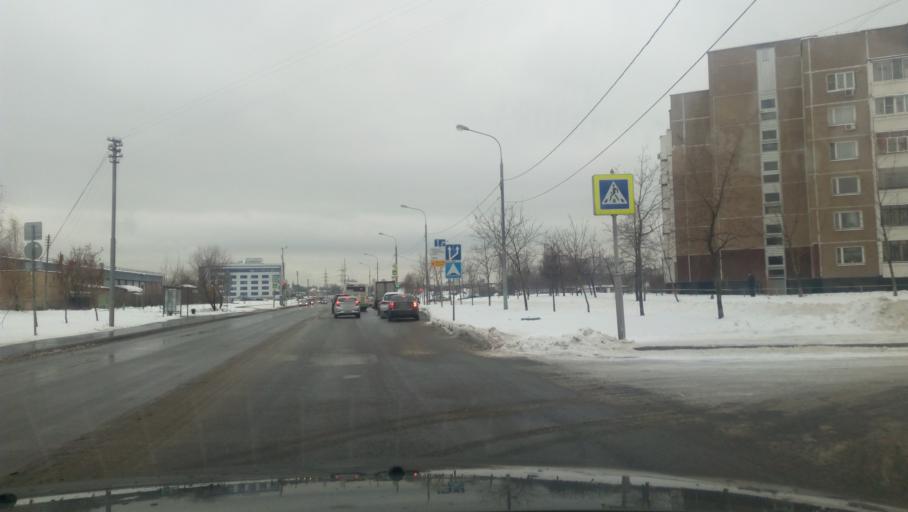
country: RU
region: Moskovskaya
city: Reutov
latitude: 55.7319
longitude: 37.8617
